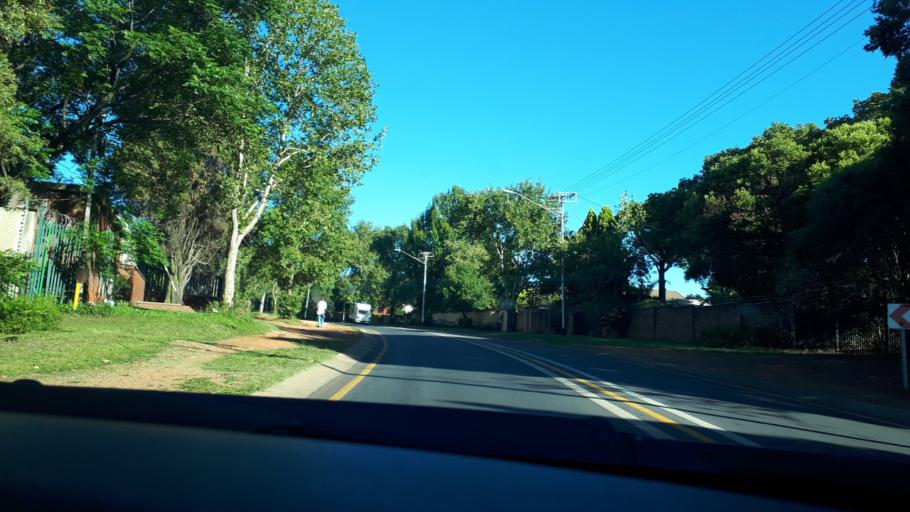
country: ZA
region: Gauteng
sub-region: City of Tshwane Metropolitan Municipality
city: Pretoria
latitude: -25.7740
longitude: 28.2821
